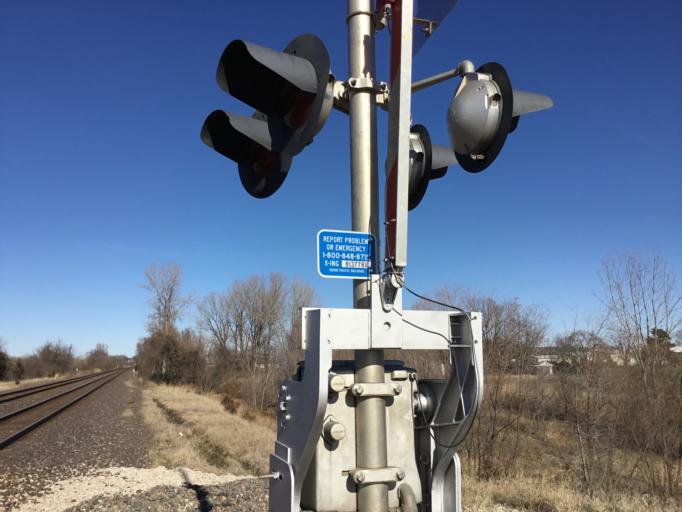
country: US
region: Kansas
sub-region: Douglas County
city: Lawrence
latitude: 39.0006
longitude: -95.2352
